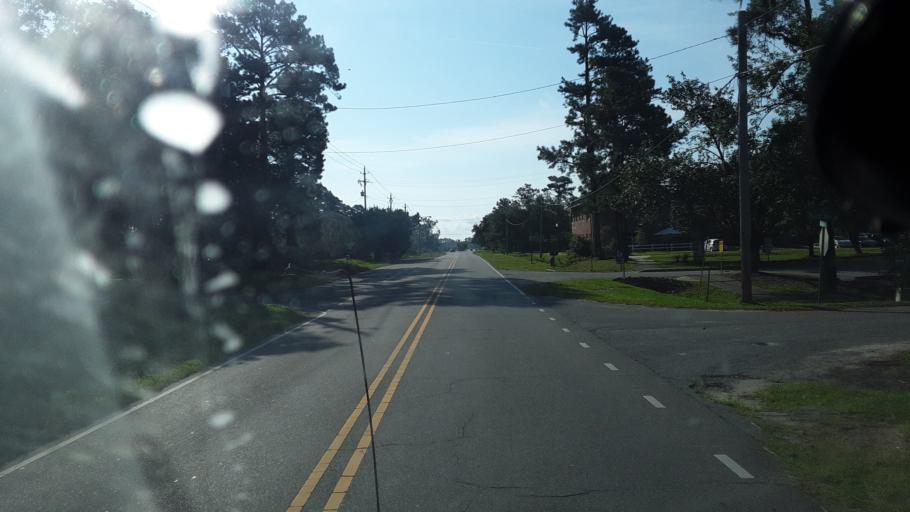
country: US
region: North Carolina
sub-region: Brunswick County
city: Navassa
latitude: 34.2398
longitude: -78.0095
